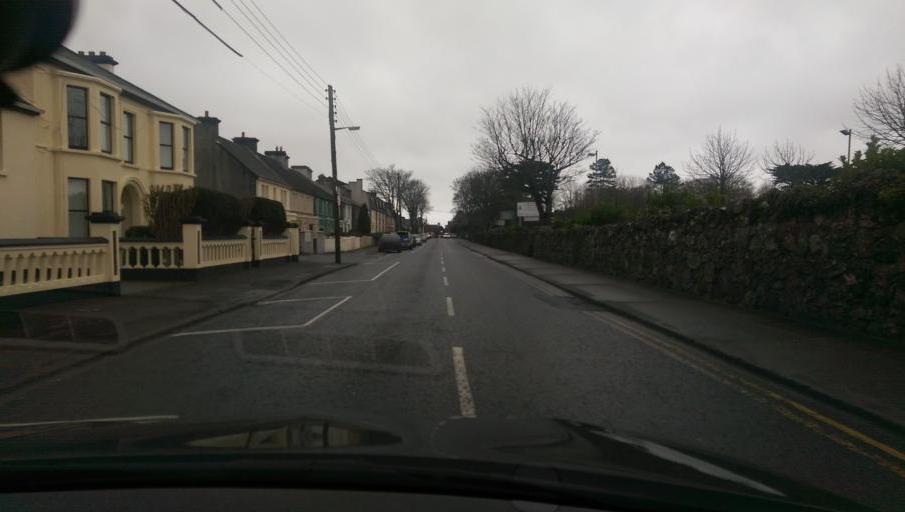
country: IE
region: Connaught
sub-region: County Galway
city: Gaillimh
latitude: 53.2712
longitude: -9.0638
